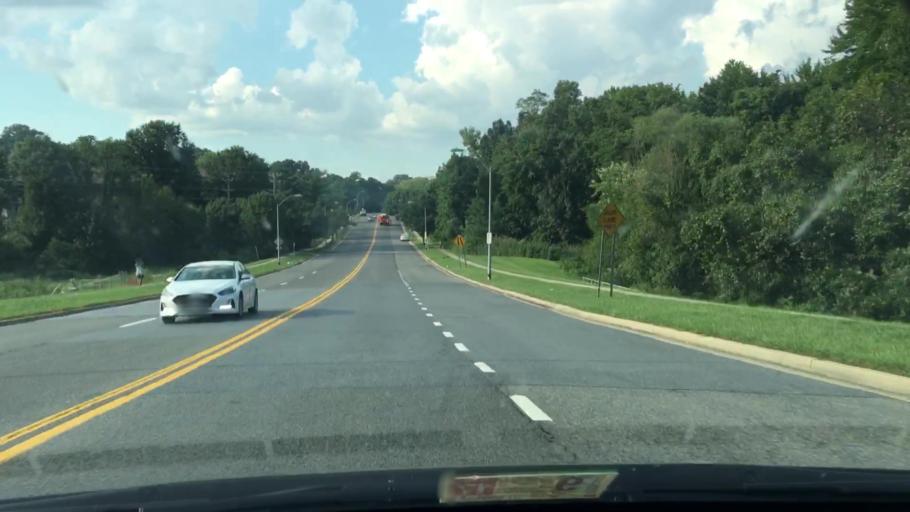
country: US
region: Maryland
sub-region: Prince George's County
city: South Laurel
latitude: 39.0582
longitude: -76.8415
